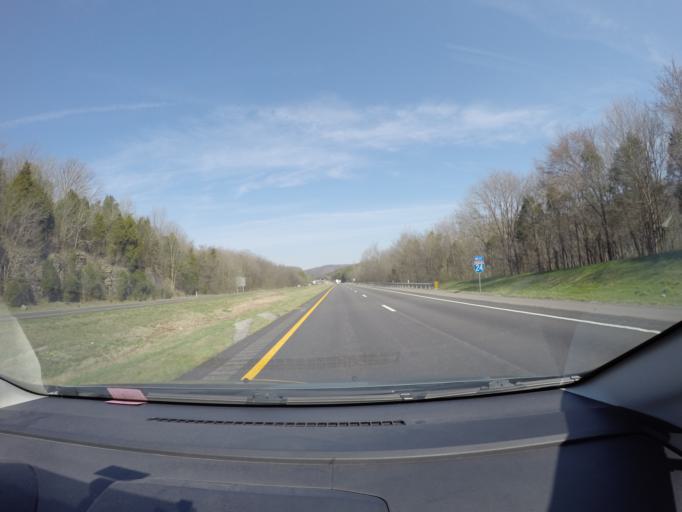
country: US
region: Tennessee
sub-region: Rutherford County
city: Plainview
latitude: 35.6290
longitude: -86.2447
